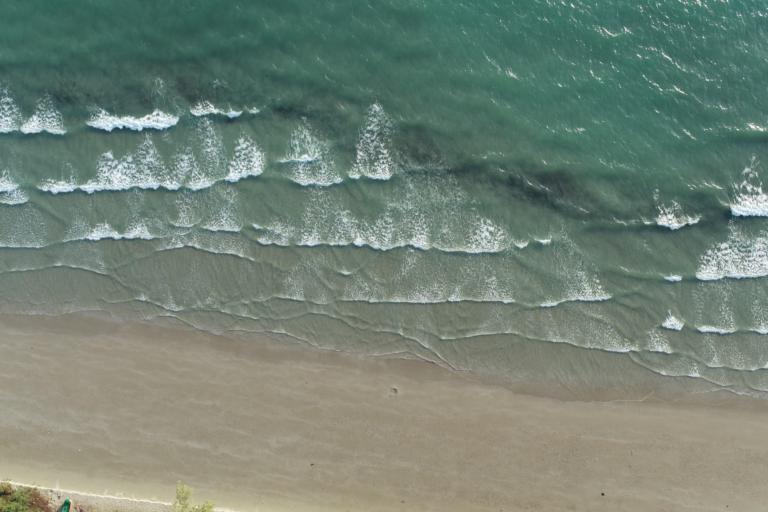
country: TH
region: Rayong
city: Rayong
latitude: 12.6007
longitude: 101.4021
